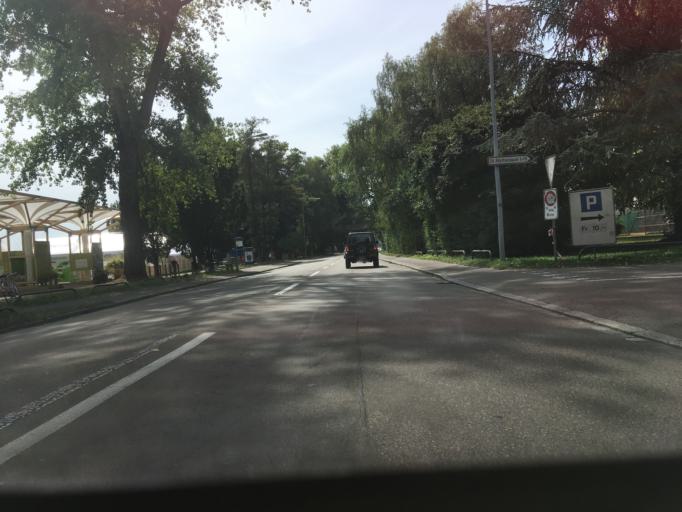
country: CH
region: Zurich
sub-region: Bezirk Zuerich
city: Zuerich (Kreis 2) / Enge
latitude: 47.3516
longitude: 8.5342
